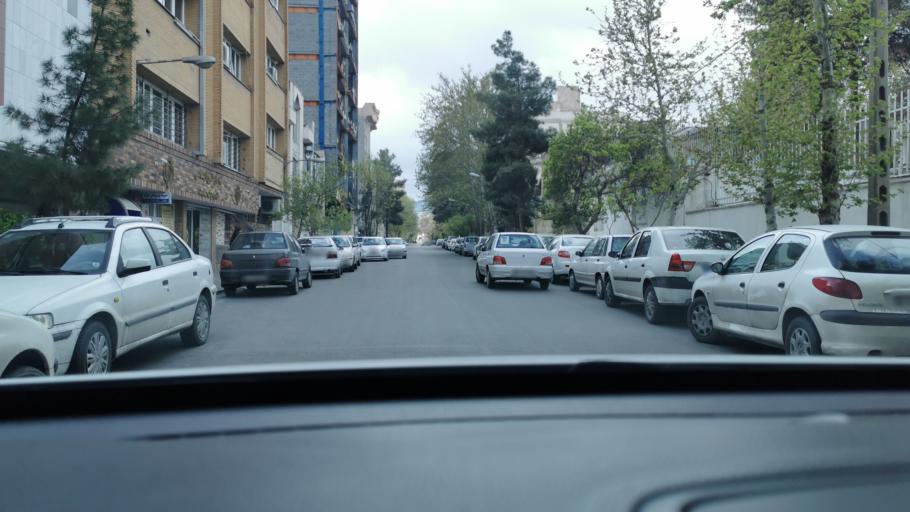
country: IR
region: Razavi Khorasan
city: Mashhad
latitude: 36.2918
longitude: 59.5604
